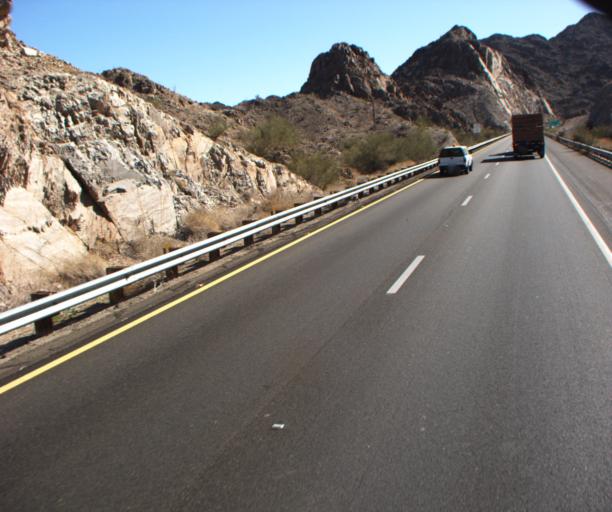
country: US
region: Arizona
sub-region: Yuma County
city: Fortuna Foothills
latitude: 32.6667
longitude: -114.3149
